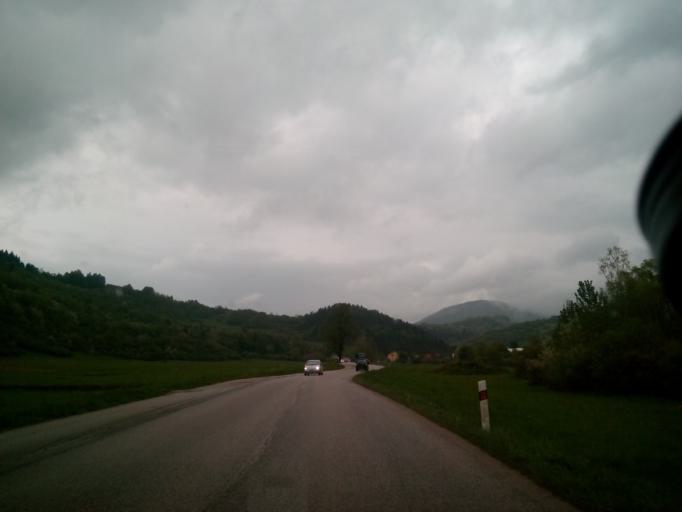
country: SK
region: Zilinsky
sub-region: Okres Zilina
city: Terchova
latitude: 49.2546
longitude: 19.0153
